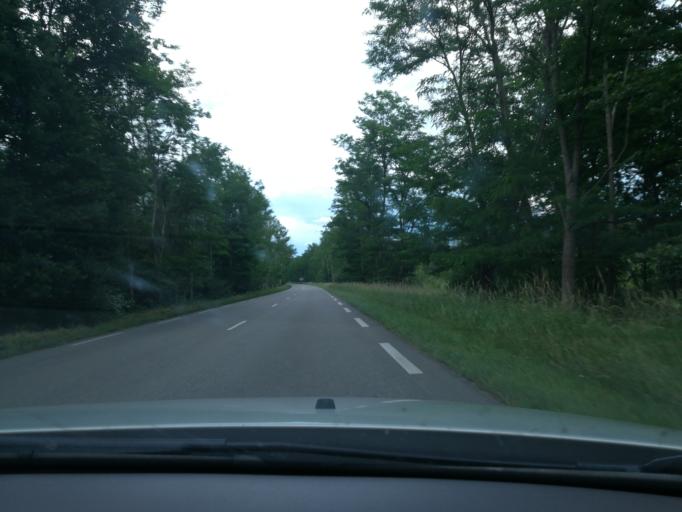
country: FR
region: Alsace
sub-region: Departement du Bas-Rhin
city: Steinbourg
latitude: 48.7633
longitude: 7.3969
